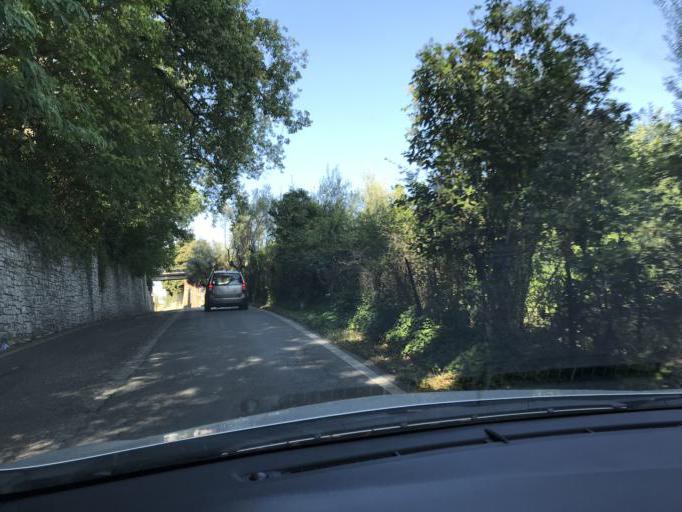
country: IT
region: Umbria
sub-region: Provincia di Perugia
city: Perugia
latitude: 43.1100
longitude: 12.4180
